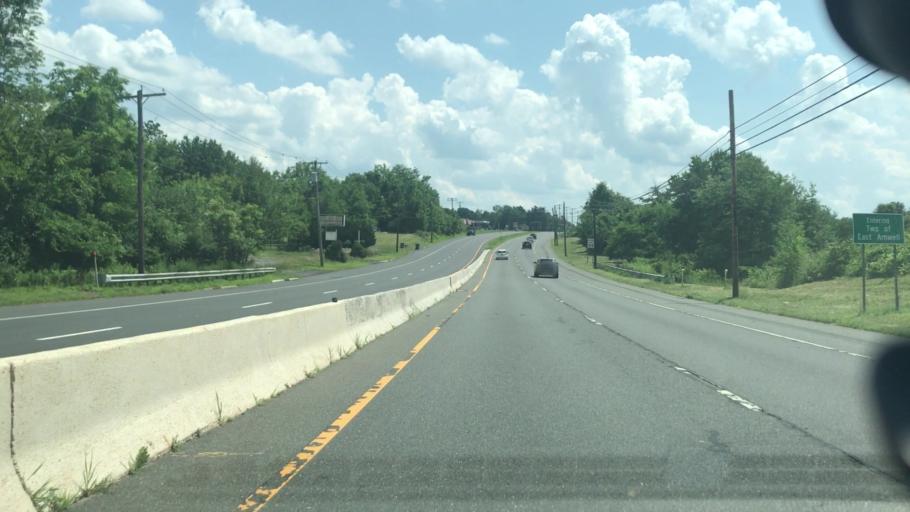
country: US
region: New Jersey
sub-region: Hunterdon County
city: Flemington
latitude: 40.4458
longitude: -74.8583
